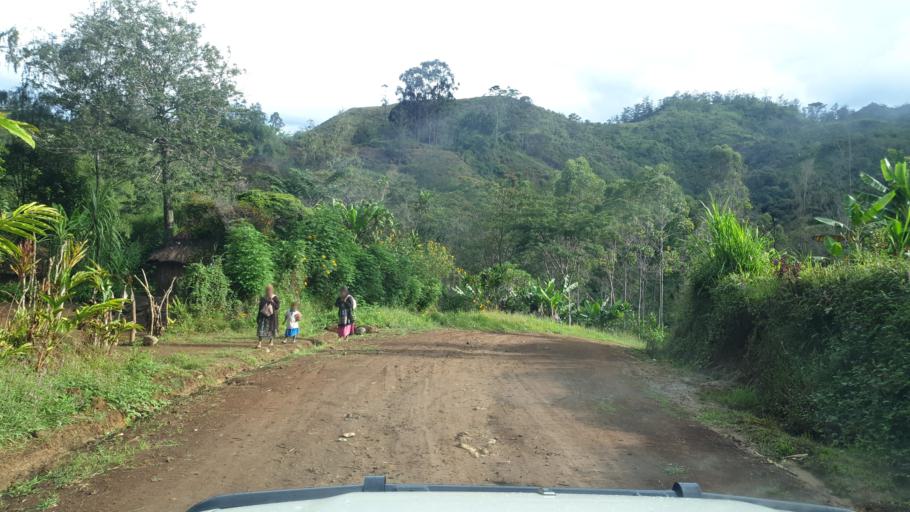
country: PG
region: Eastern Highlands
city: Goroka
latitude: -5.9186
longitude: 145.2557
